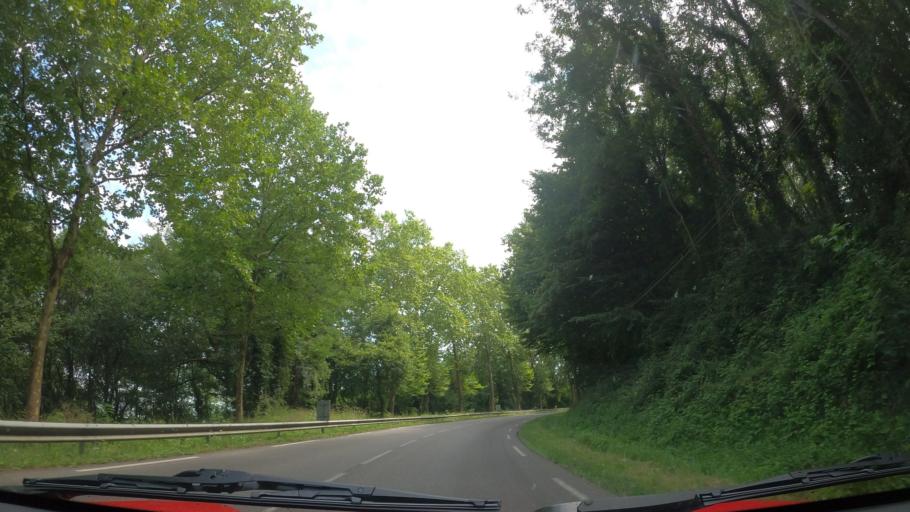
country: FR
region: Aquitaine
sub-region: Departement des Landes
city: Peyrehorade
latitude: 43.5303
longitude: -1.1069
